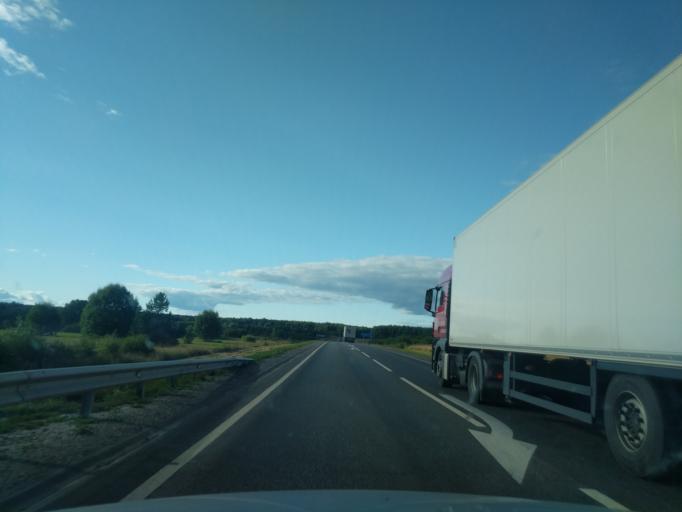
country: RU
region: Kostroma
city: Manturovo
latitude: 58.3062
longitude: 44.7258
